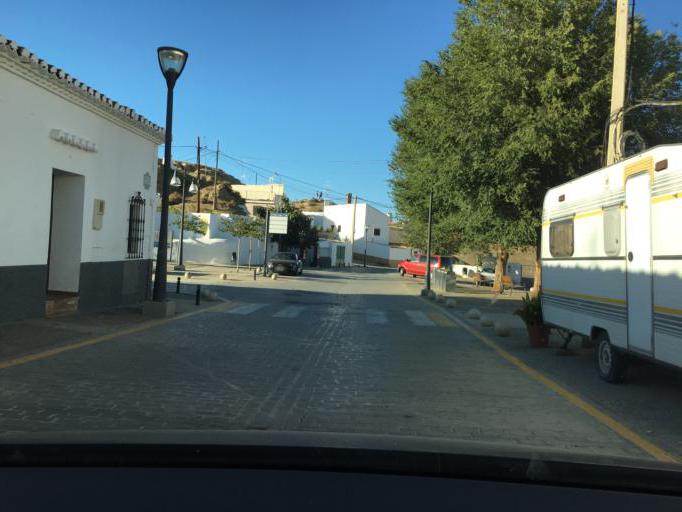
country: ES
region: Andalusia
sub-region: Provincia de Granada
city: Guadix
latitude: 37.2943
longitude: -3.1419
